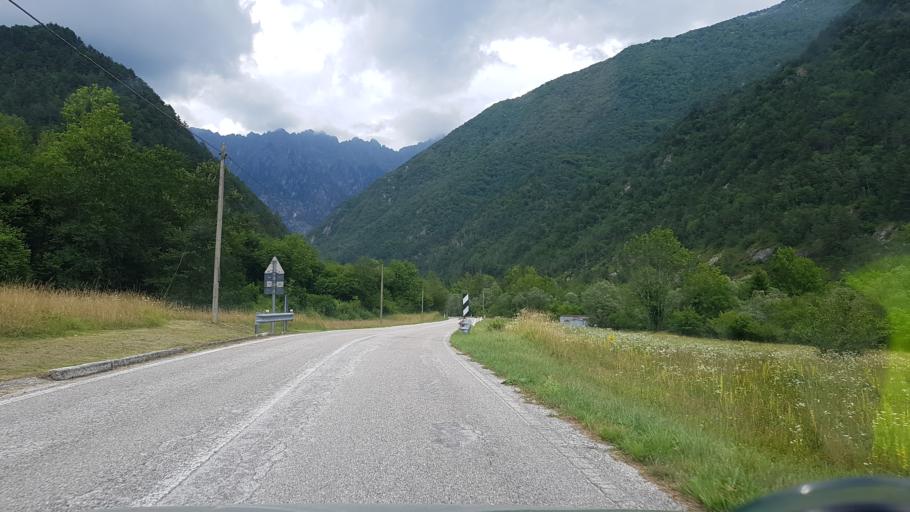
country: IT
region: Friuli Venezia Giulia
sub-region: Provincia di Udine
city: Lusevera
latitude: 46.2836
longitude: 13.2656
